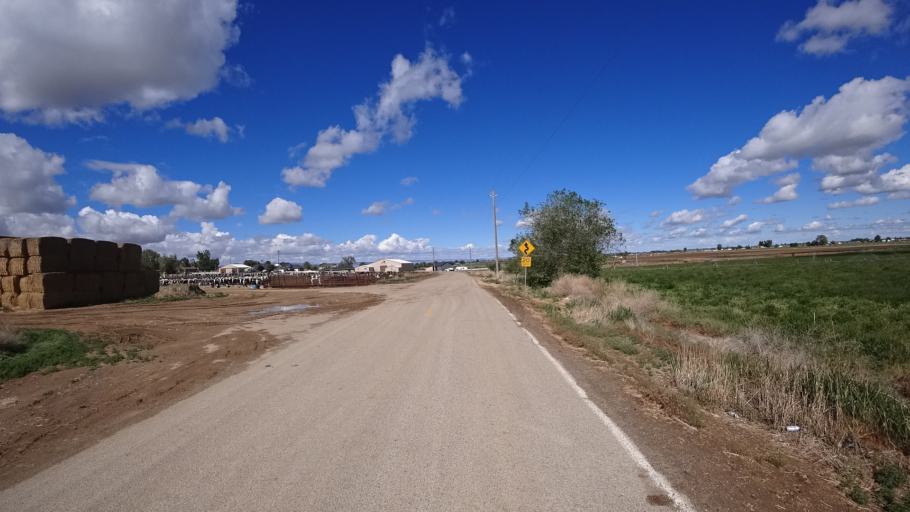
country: US
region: Idaho
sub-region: Ada County
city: Kuna
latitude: 43.4665
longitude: -116.4616
